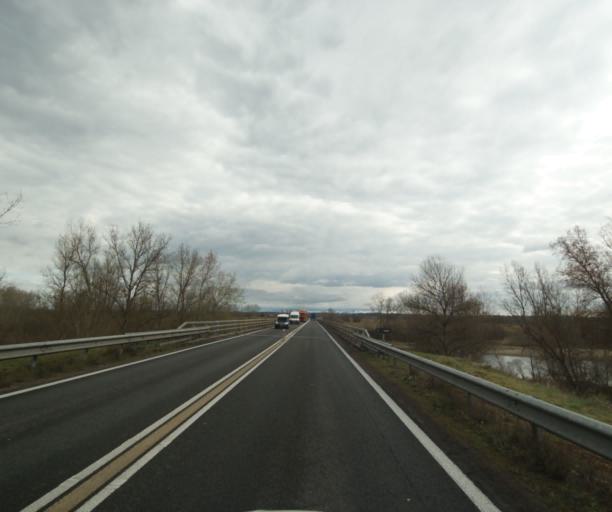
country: FR
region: Auvergne
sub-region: Departement de l'Allier
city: Bessay-sur-Allier
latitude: 46.4793
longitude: 3.3282
